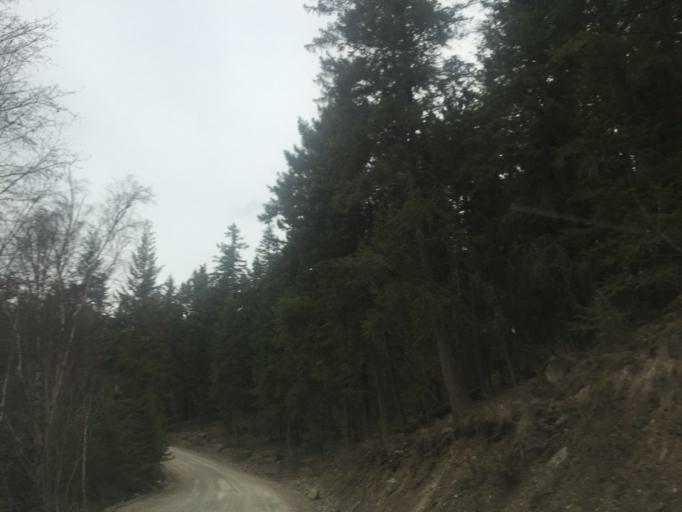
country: CA
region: British Columbia
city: Kamloops
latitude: 51.3675
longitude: -120.1549
